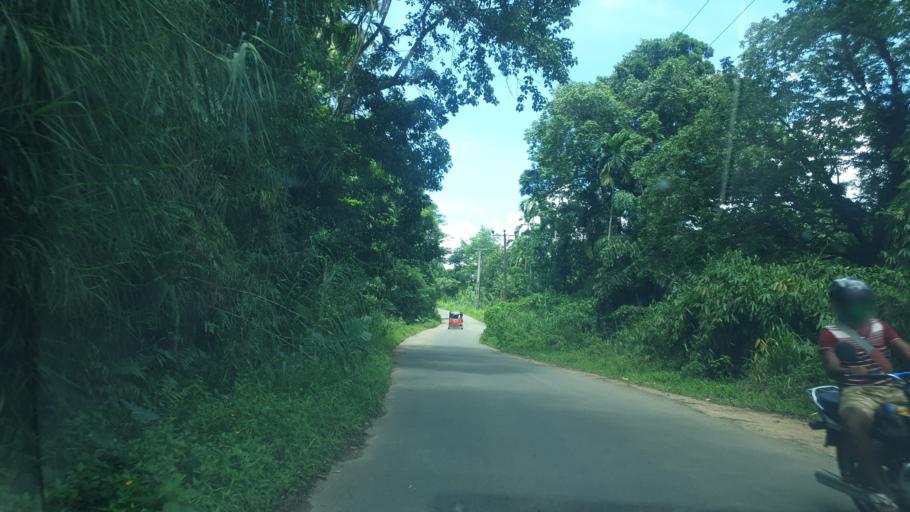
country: LK
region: Sabaragamuwa
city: Ratnapura
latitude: 6.4826
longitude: 80.4095
